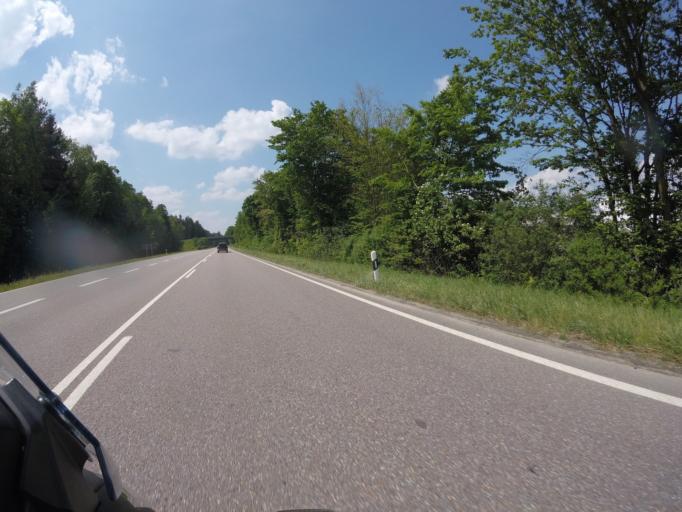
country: DE
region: Bavaria
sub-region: Upper Bavaria
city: Munchsmunster
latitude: 48.7550
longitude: 11.7058
